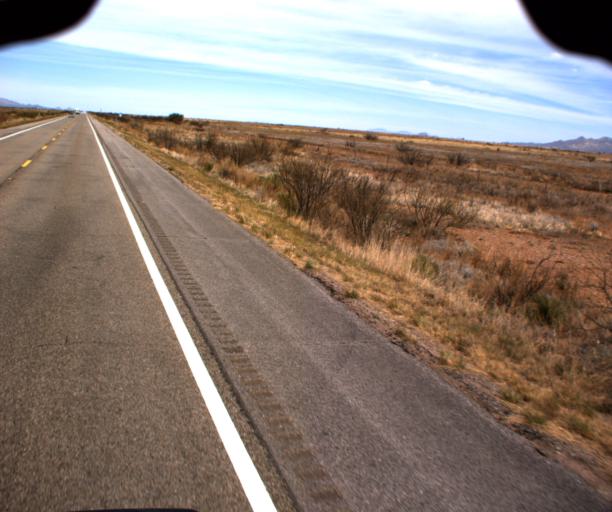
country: US
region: Arizona
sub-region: Cochise County
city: Pirtleville
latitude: 31.5102
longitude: -109.6404
